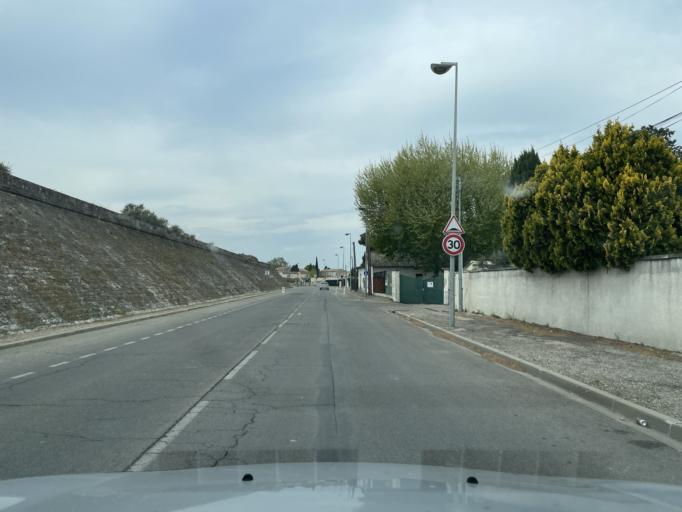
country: FR
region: Provence-Alpes-Cote d'Azur
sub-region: Departement des Bouches-du-Rhone
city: Tarascon
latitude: 43.8107
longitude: 4.6647
